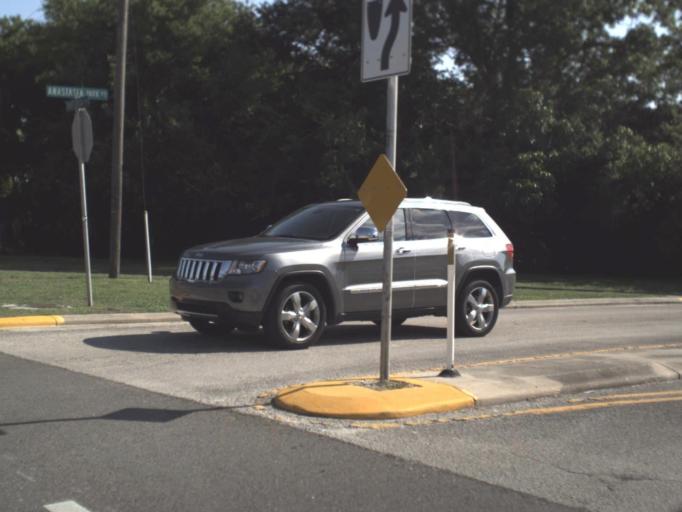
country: US
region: Florida
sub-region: Saint Johns County
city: Saint Augustine
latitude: 29.8805
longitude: -81.2865
